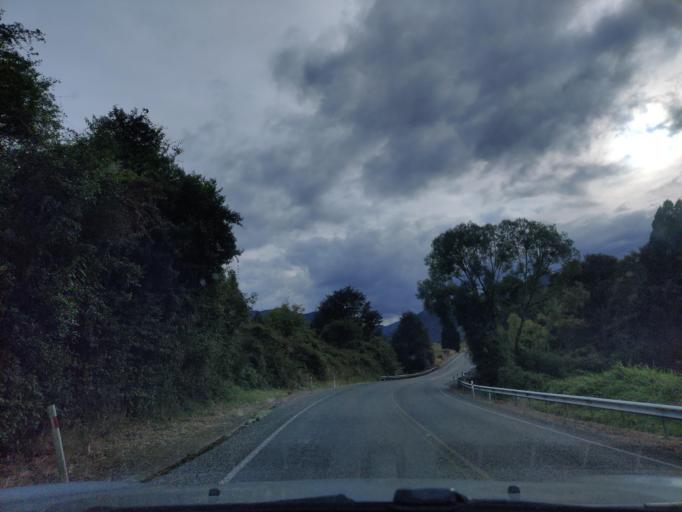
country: NZ
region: Tasman
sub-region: Tasman District
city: Wakefield
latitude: -41.7125
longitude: 172.4128
